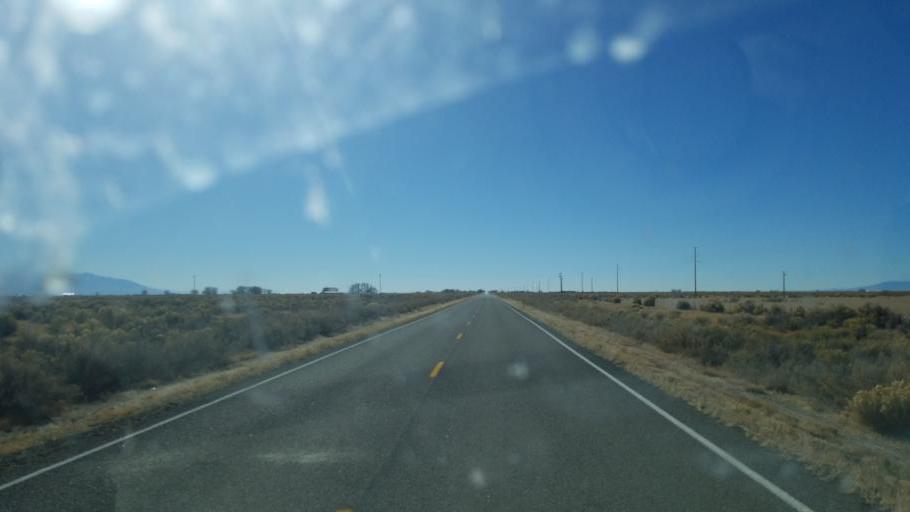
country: US
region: Colorado
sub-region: Saguache County
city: Saguache
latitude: 38.0518
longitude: -105.9144
